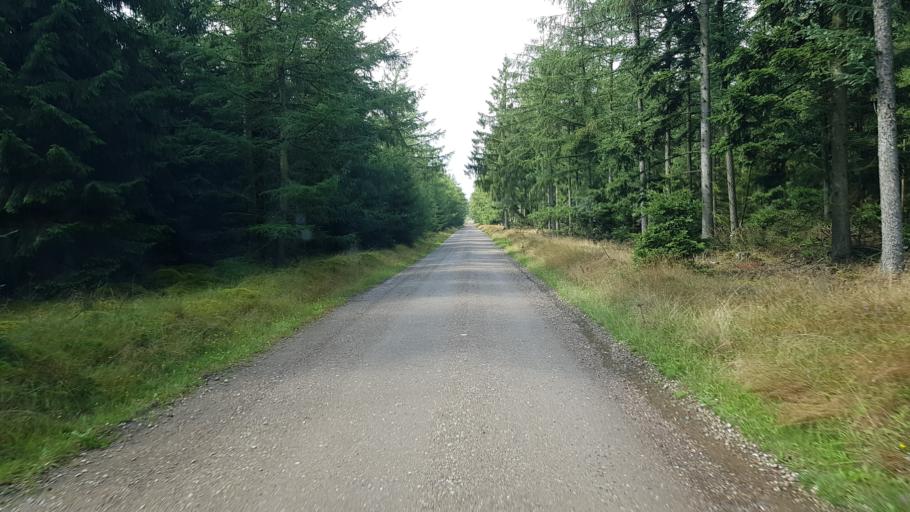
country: DK
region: South Denmark
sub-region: Vejen Kommune
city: Holsted
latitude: 55.5954
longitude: 8.8945
